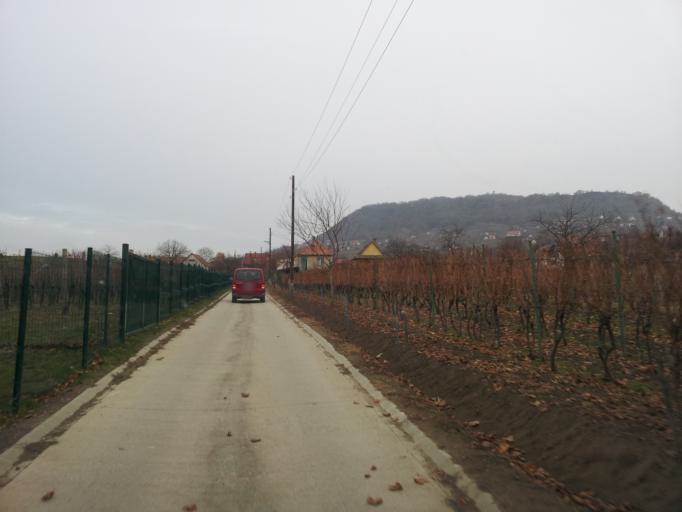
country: HU
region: Veszprem
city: Devecser
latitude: 47.1311
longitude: 17.3714
